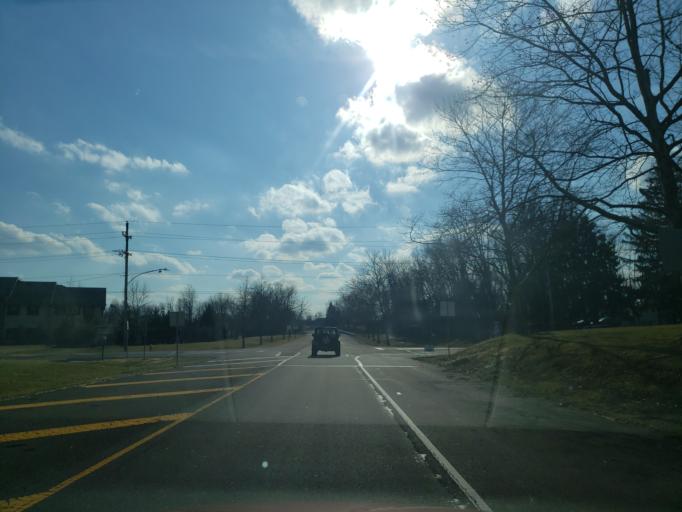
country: US
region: Pennsylvania
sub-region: Bucks County
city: Doylestown
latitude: 40.2914
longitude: -75.1286
